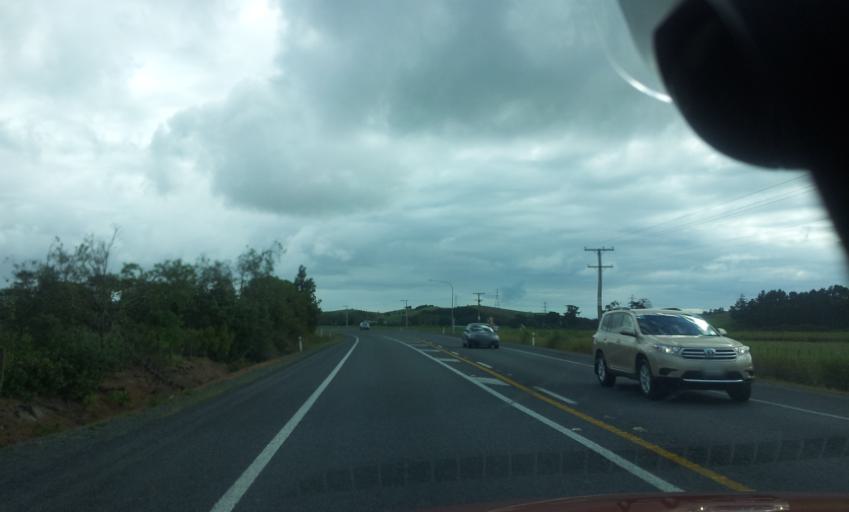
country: NZ
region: Northland
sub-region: Whangarei
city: Ruakaka
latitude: -36.0217
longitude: 174.4183
